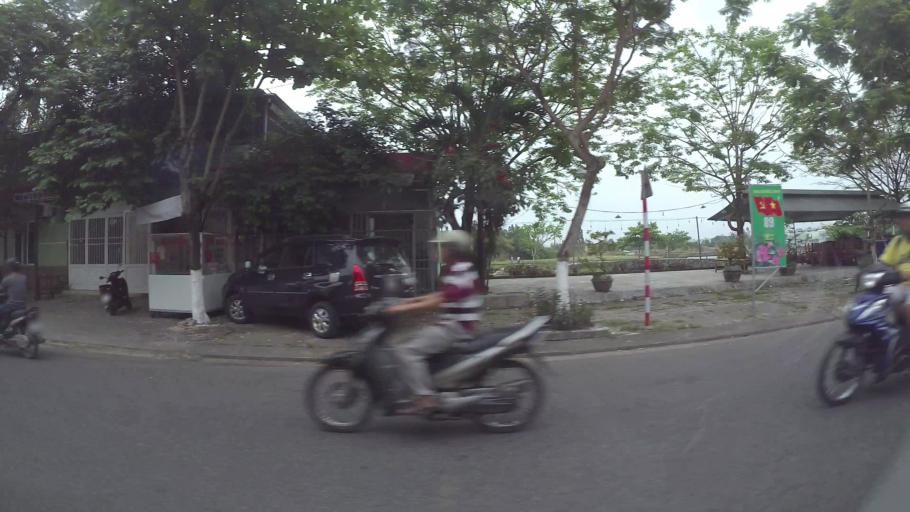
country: VN
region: Da Nang
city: Thanh Khe
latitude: 16.0612
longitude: 108.1914
